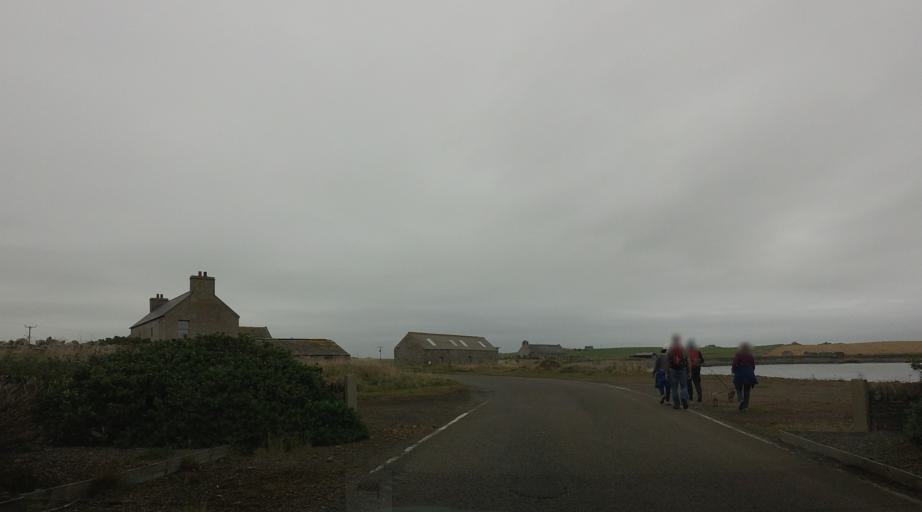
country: GB
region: Scotland
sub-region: Orkney Islands
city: Orkney
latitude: 58.7413
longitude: -2.9721
